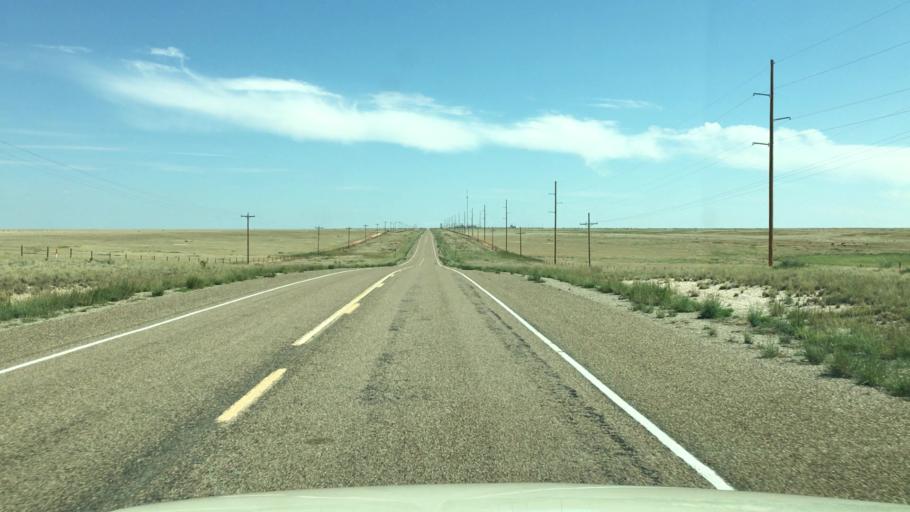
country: US
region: New Mexico
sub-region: Chaves County
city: Roswell
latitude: 33.9468
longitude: -104.5899
